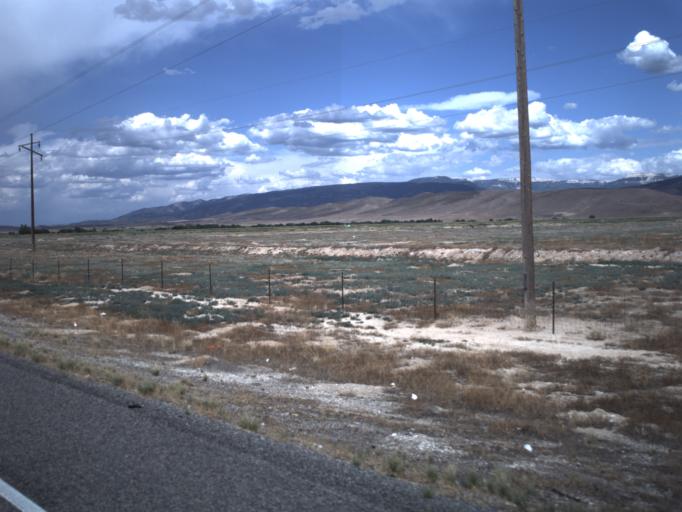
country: US
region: Utah
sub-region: Sevier County
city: Salina
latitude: 39.0305
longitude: -111.8298
